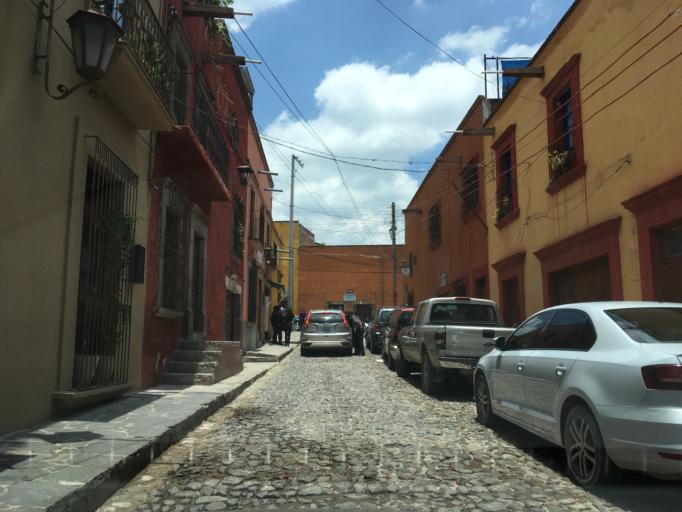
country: MX
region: Guanajuato
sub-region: San Miguel de Allende
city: San Miguel de Allende
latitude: 20.9147
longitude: -100.7479
